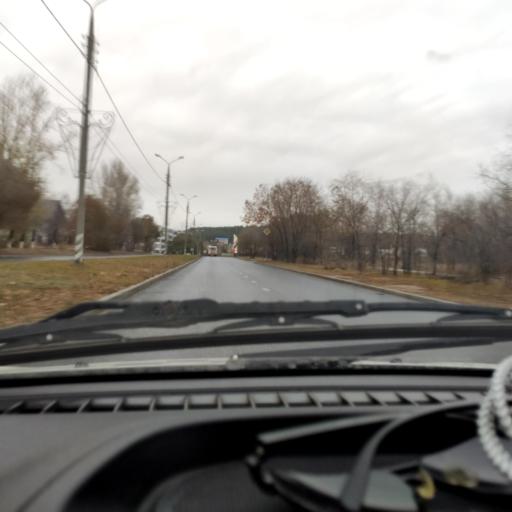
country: RU
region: Samara
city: Zhigulevsk
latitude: 53.4687
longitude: 49.5371
